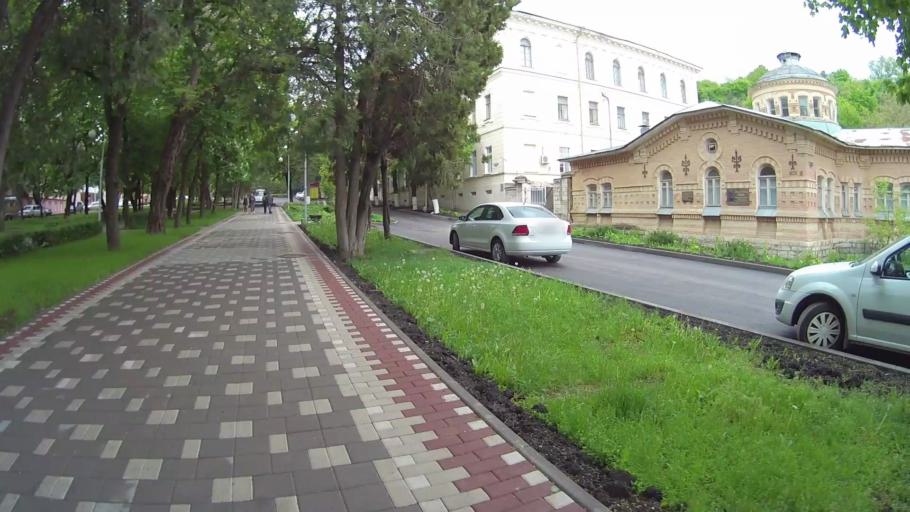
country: RU
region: Stavropol'skiy
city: Goryachevodskiy
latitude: 44.0371
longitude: 43.0826
